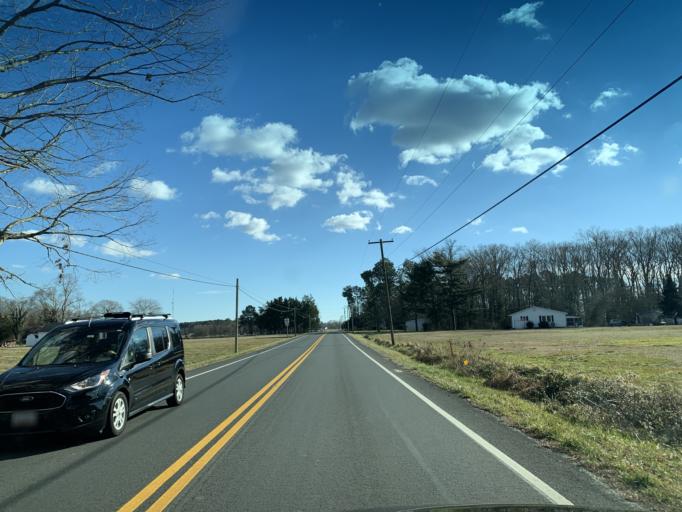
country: US
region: Maryland
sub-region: Worcester County
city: Berlin
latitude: 38.3554
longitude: -75.1963
